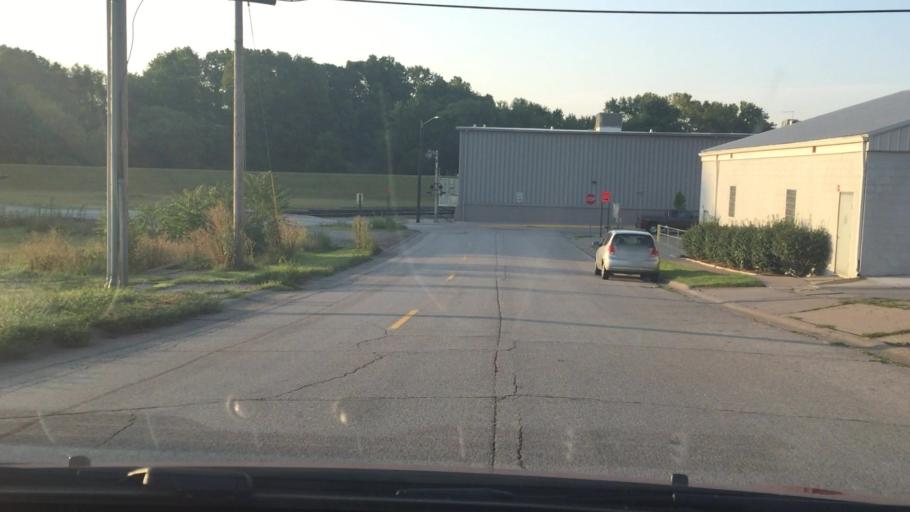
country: US
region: Iowa
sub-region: Muscatine County
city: Muscatine
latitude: 41.4295
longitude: -91.0391
